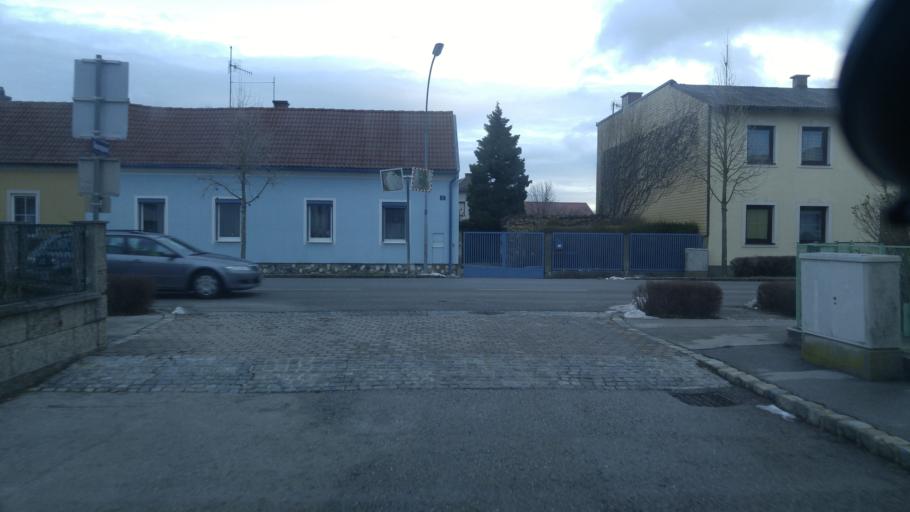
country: AT
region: Lower Austria
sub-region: Politischer Bezirk Baden
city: Bad Voslau
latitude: 47.9609
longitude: 16.1913
